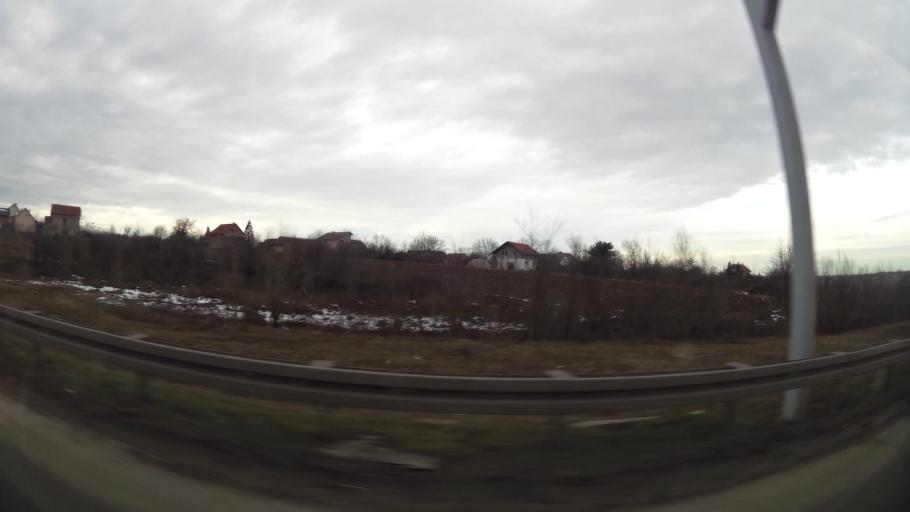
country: RS
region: Central Serbia
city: Sremcica
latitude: 44.7109
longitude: 20.3789
